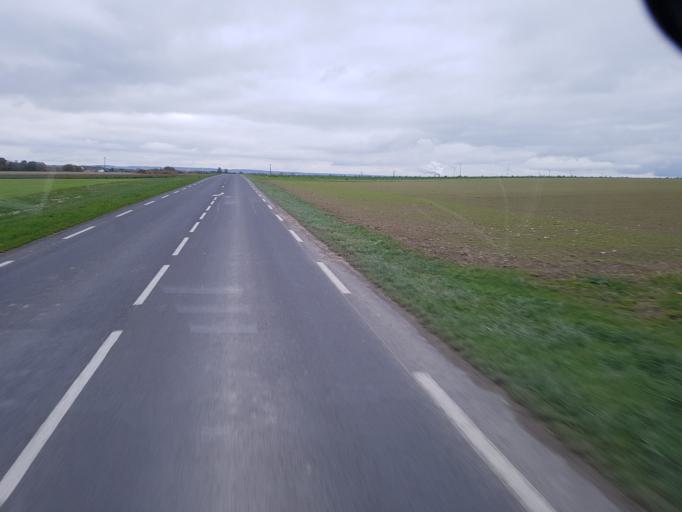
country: FR
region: Champagne-Ardenne
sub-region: Departement de la Marne
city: Saint-Just-Sauvage
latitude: 48.5840
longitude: 3.8443
